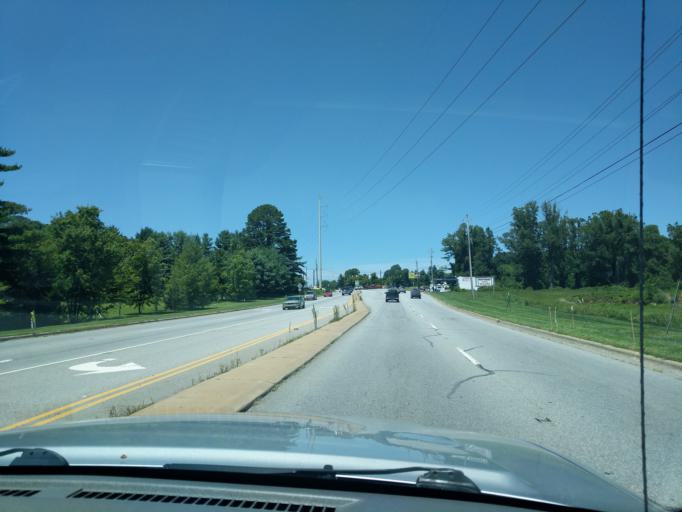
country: US
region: North Carolina
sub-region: Buncombe County
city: Royal Pines
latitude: 35.4576
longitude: -82.5113
